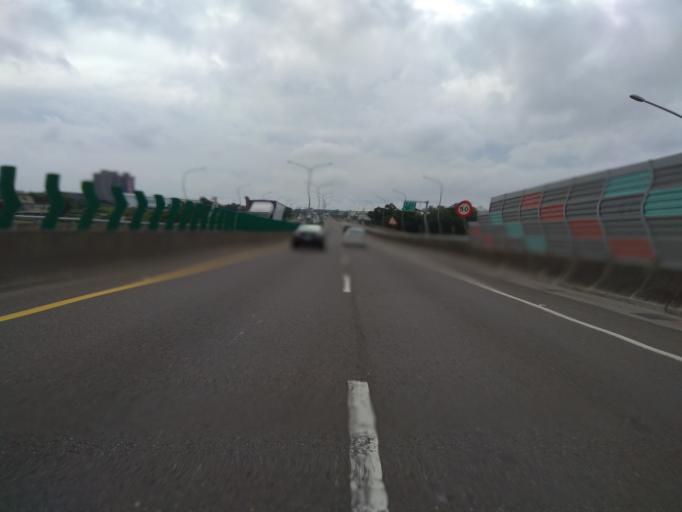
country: TW
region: Taiwan
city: Taoyuan City
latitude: 24.9470
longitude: 121.1665
